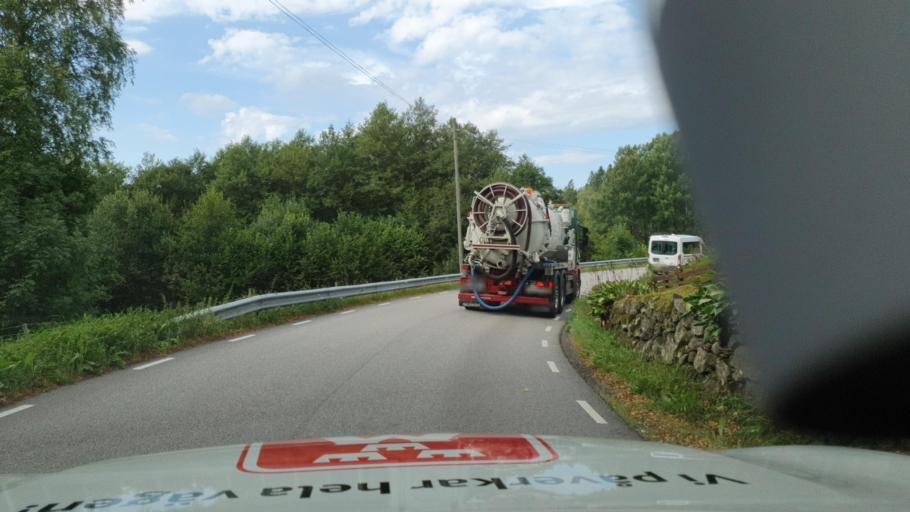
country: SE
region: Vaestra Goetaland
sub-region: Marks Kommun
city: Kinna
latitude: 57.4258
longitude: 12.6795
